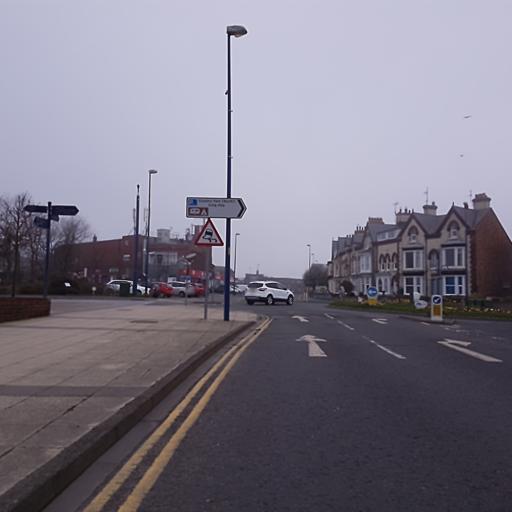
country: GB
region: England
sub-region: North Yorkshire
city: Filey
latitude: 54.2102
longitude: -0.2913
